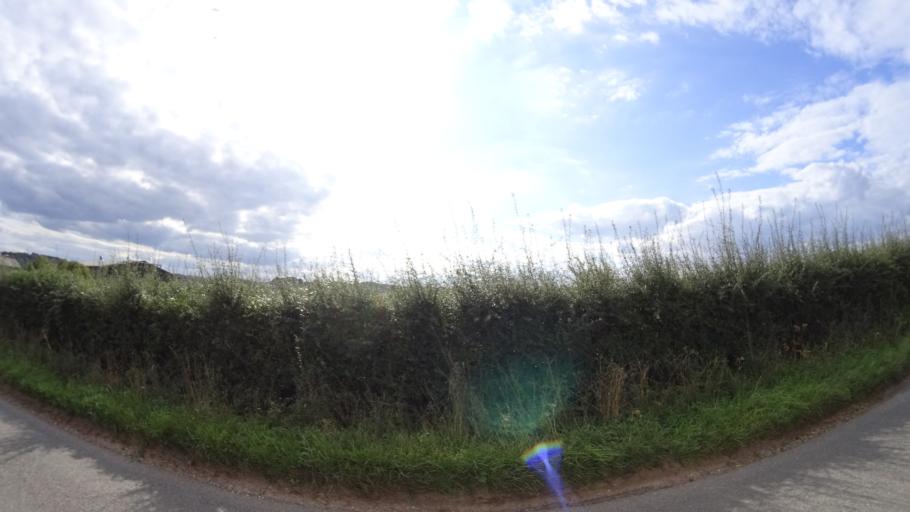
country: GB
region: England
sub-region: Hampshire
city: East Dean
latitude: 51.1056
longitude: -1.5742
